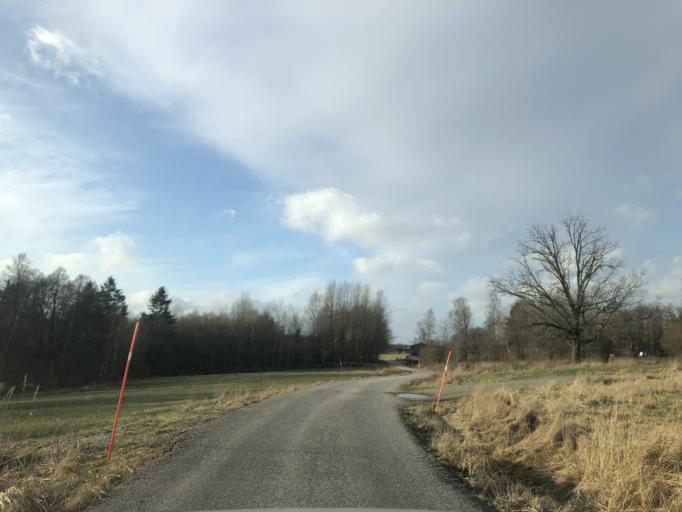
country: SE
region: Vaestra Goetaland
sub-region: Ulricehamns Kommun
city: Ulricehamn
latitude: 57.8087
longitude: 13.3633
